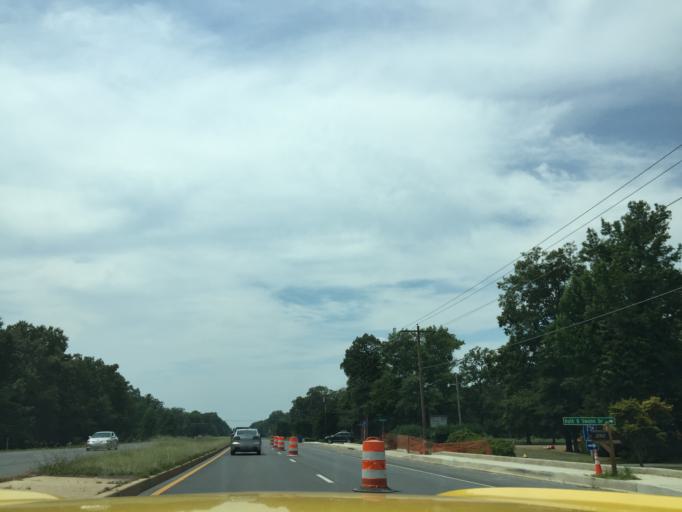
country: US
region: Maryland
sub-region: Charles County
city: Bryans Road
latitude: 38.6225
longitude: -77.0847
